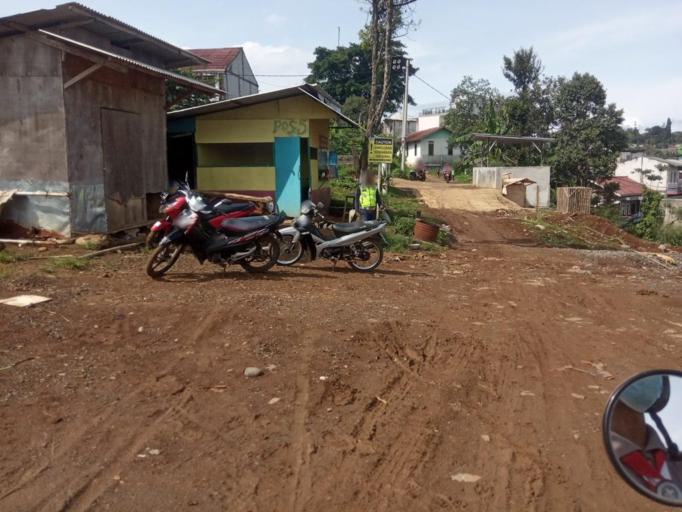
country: ID
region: West Java
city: Caringin
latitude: -6.6611
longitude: 106.8792
